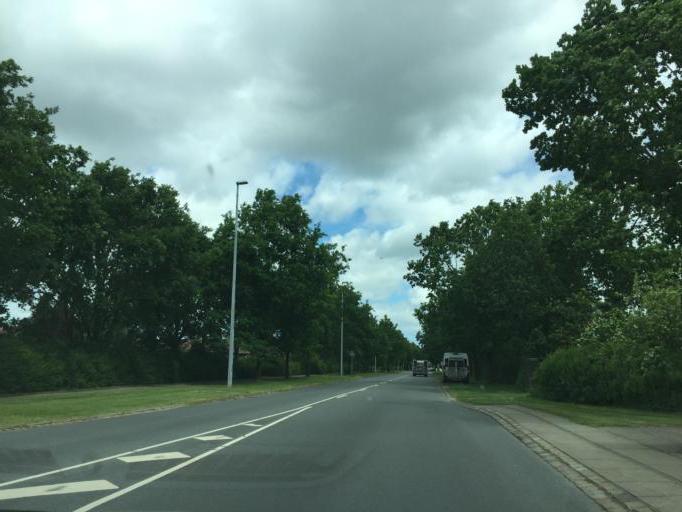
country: DK
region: South Denmark
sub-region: Odense Kommune
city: Neder Holluf
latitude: 55.3616
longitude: 10.4488
